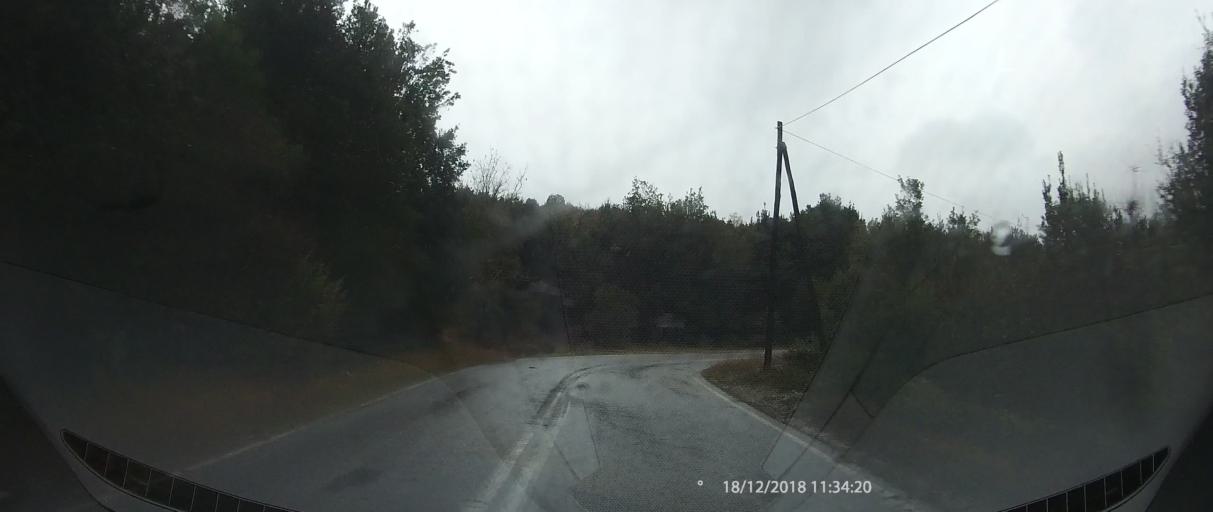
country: GR
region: Central Macedonia
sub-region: Nomos Pierias
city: Litochoro
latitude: 40.1156
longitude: 22.4888
